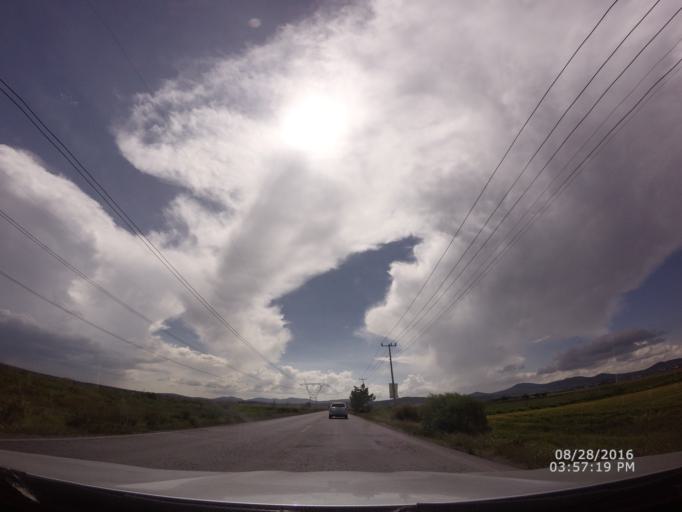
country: MX
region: Hidalgo
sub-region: Mineral de la Reforma
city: Forjadores de Pachuca
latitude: 20.0354
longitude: -98.7658
